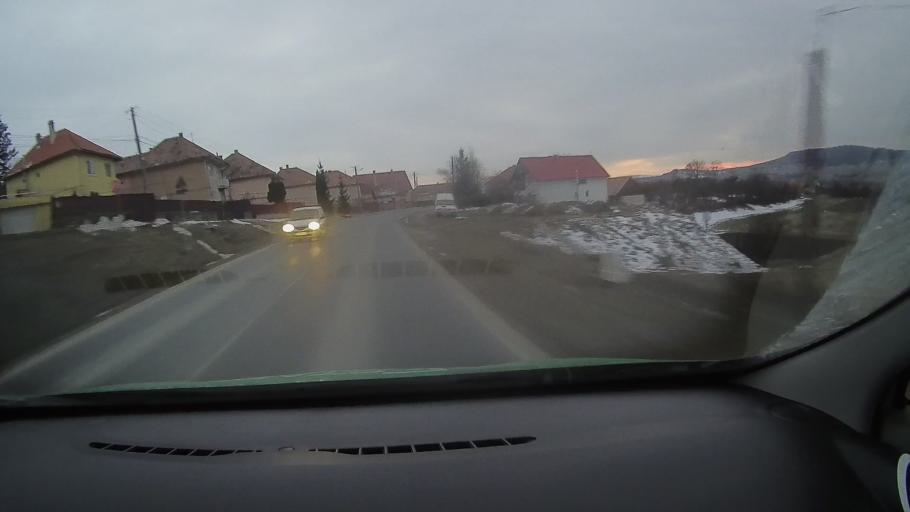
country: RO
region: Harghita
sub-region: Comuna Feliceni
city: Feliceni
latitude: 46.2758
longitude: 25.2846
